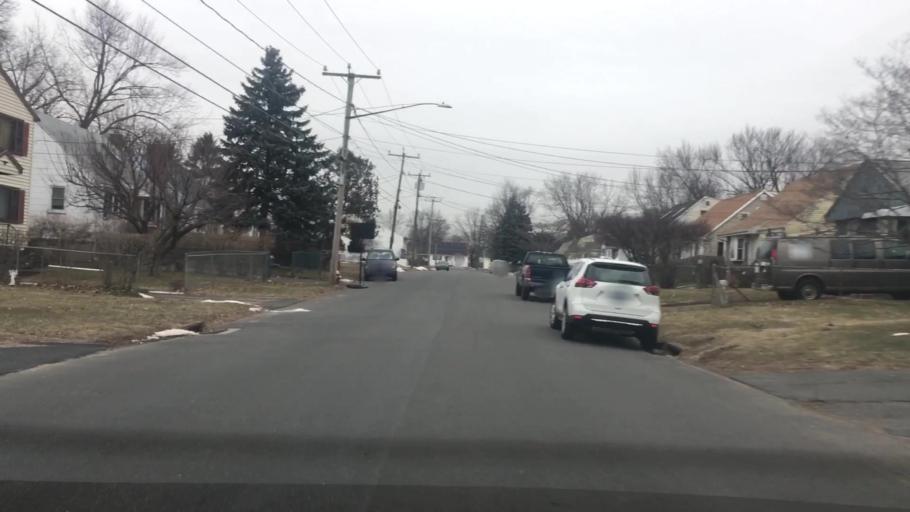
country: US
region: Connecticut
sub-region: Hartford County
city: Kensington
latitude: 41.6521
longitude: -72.7551
